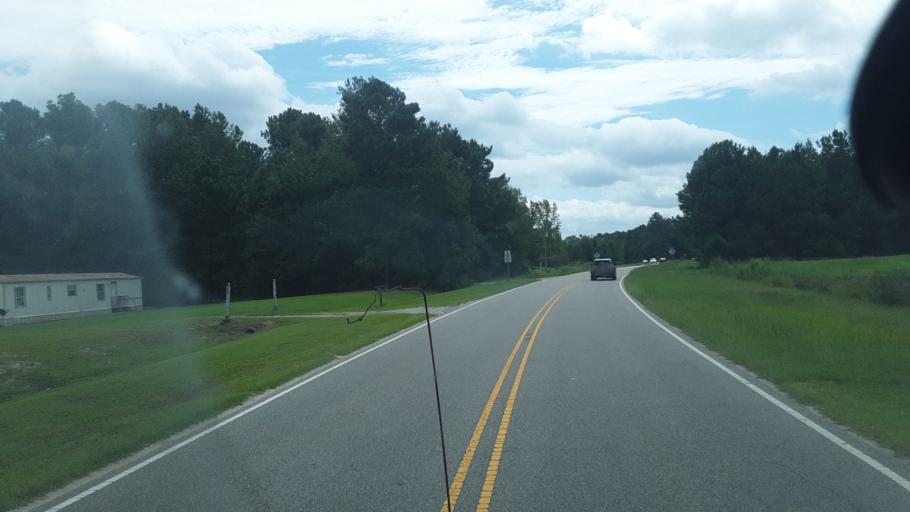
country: US
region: North Carolina
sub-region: Robeson County
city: Fairmont
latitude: 34.3989
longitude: -79.1248
